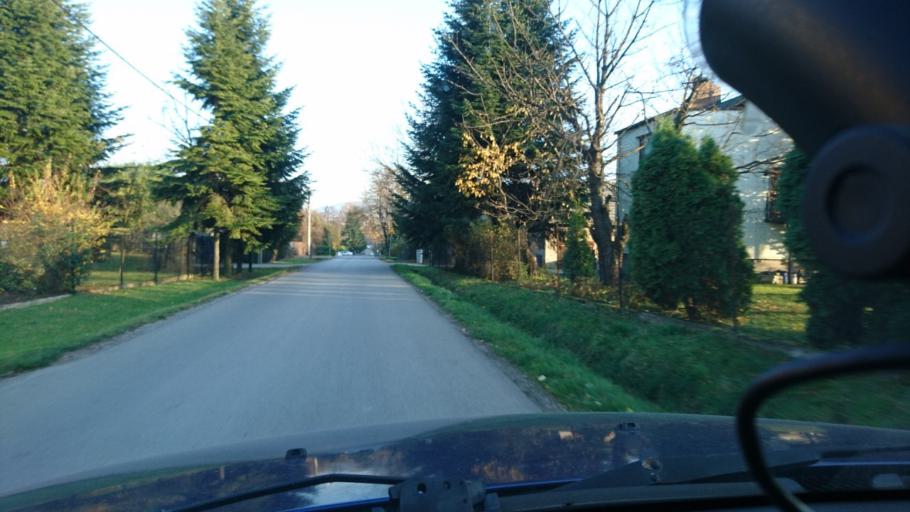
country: PL
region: Silesian Voivodeship
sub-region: Powiat bielski
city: Mazancowice
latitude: 49.8628
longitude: 19.0220
